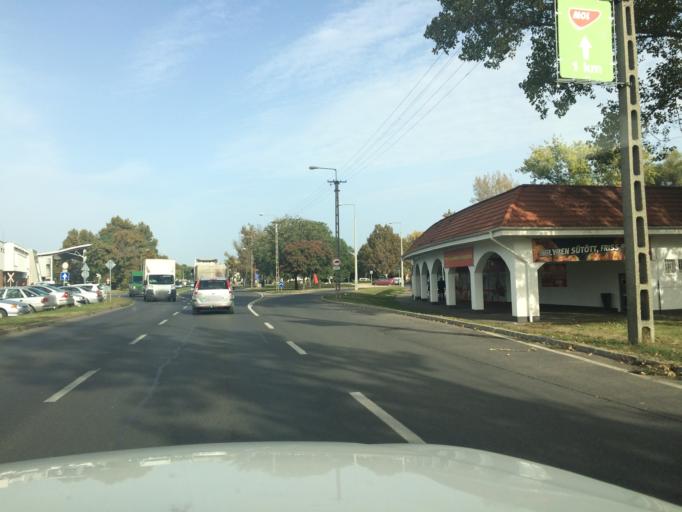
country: HU
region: Szabolcs-Szatmar-Bereg
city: Nyiregyhaza
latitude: 47.9449
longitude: 21.7074
